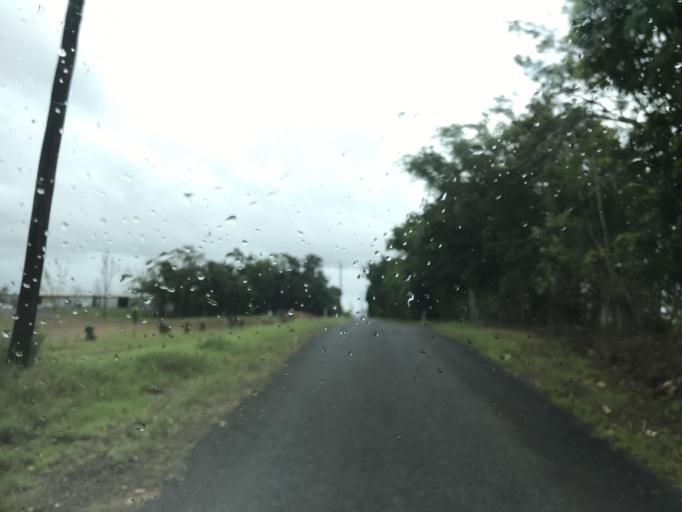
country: AU
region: Queensland
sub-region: Cassowary Coast
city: Innisfail
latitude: -17.4865
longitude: 145.9889
